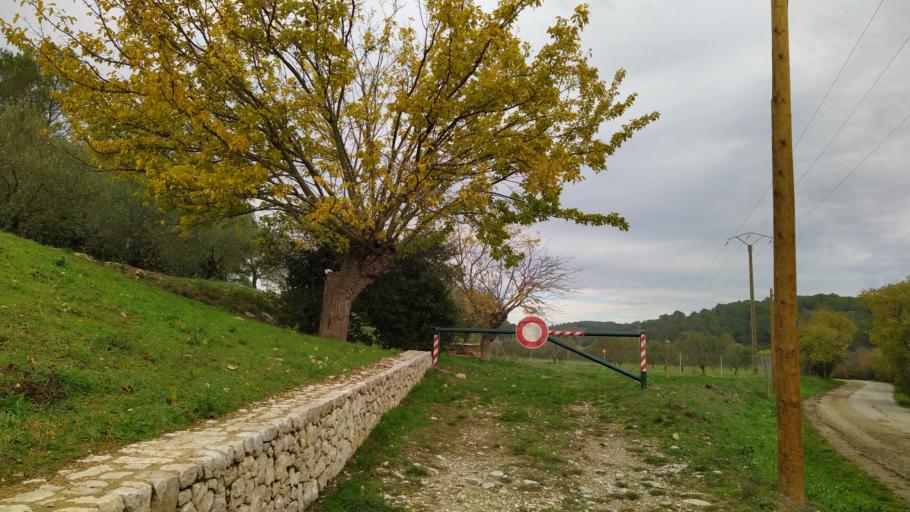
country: FR
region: Languedoc-Roussillon
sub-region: Departement du Gard
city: Poulx
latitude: 43.8720
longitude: 4.4057
